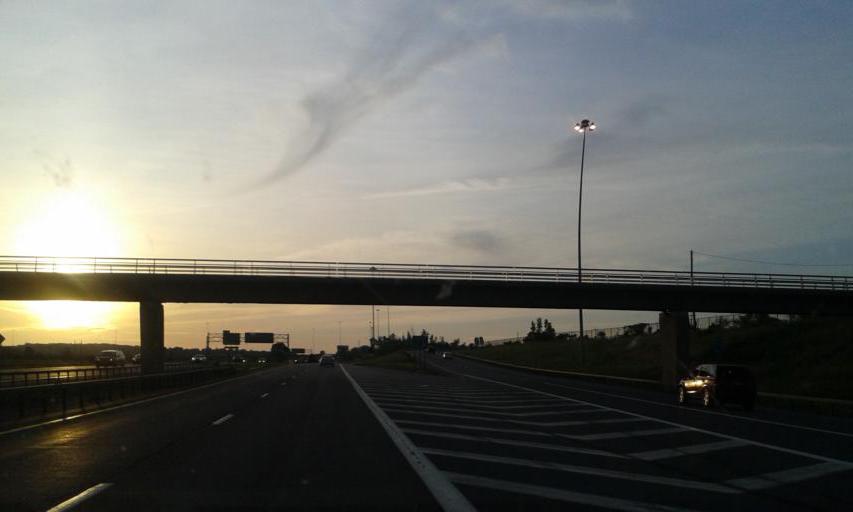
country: US
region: New York
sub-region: Onondaga County
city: Solvay
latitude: 43.0745
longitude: -76.2113
